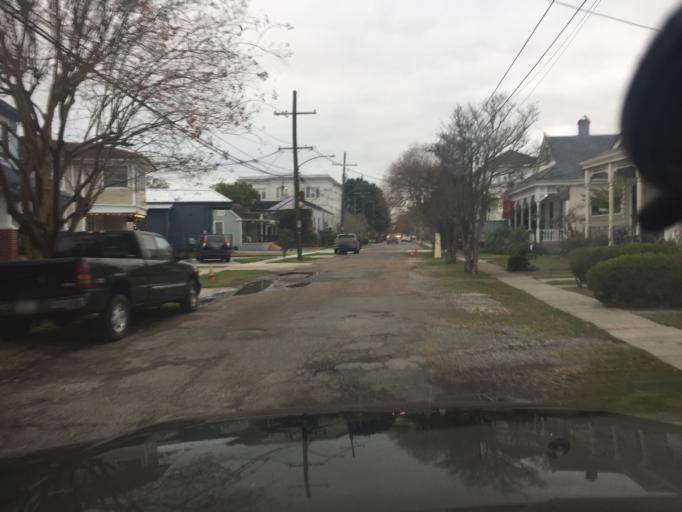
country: US
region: Louisiana
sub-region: Orleans Parish
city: New Orleans
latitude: 29.9794
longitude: -90.0797
